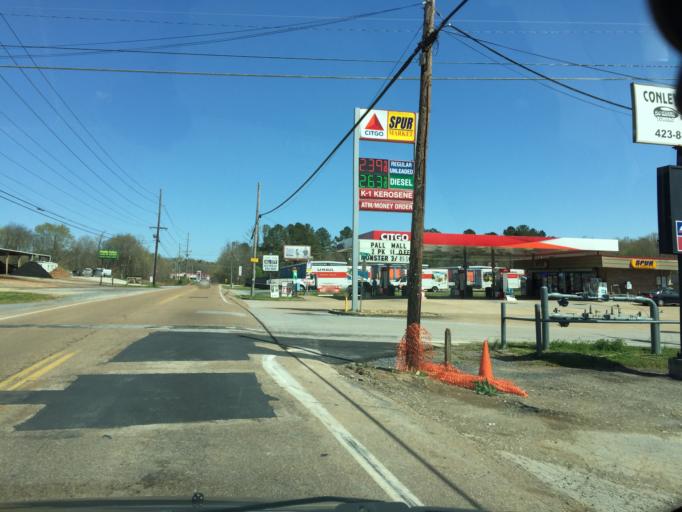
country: US
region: Tennessee
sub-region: Hamilton County
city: Middle Valley
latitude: 35.1681
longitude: -85.2092
